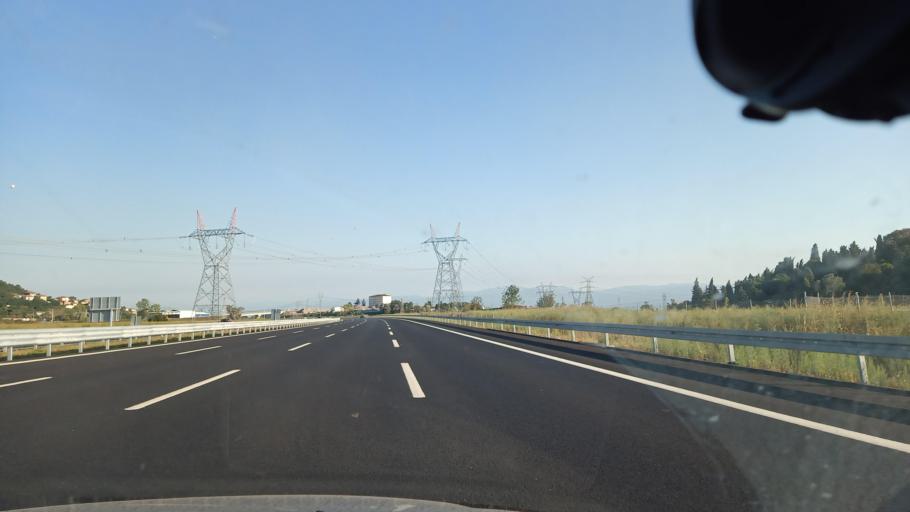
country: TR
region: Sakarya
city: Adapazari
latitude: 40.8309
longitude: 30.3894
